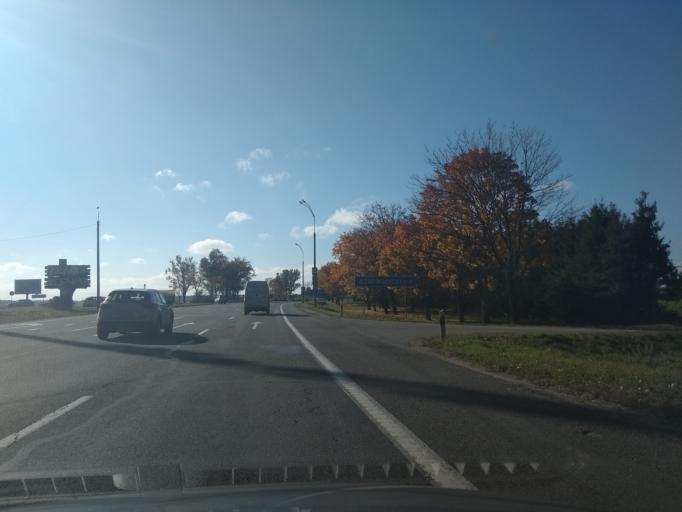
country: BY
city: Fanipol
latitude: 53.7821
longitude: 27.3623
